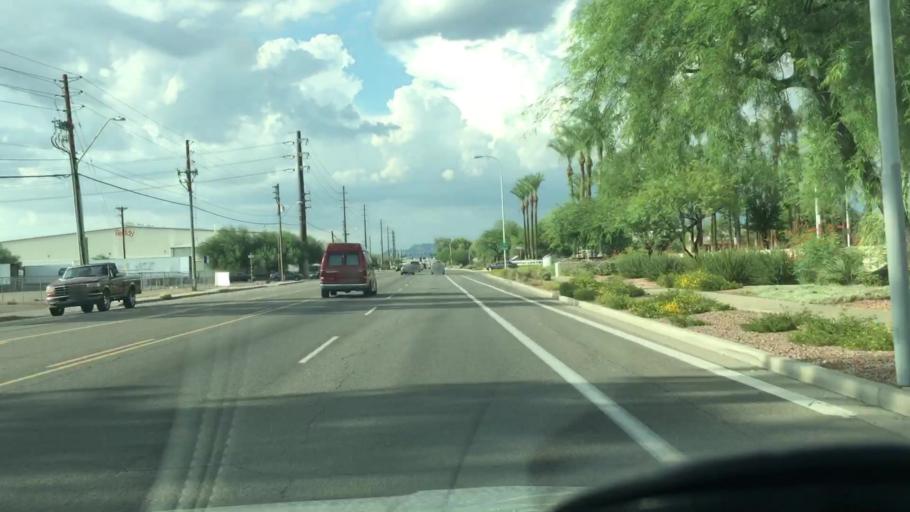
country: US
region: Arizona
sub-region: Maricopa County
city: Guadalupe
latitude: 33.4025
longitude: -111.9954
